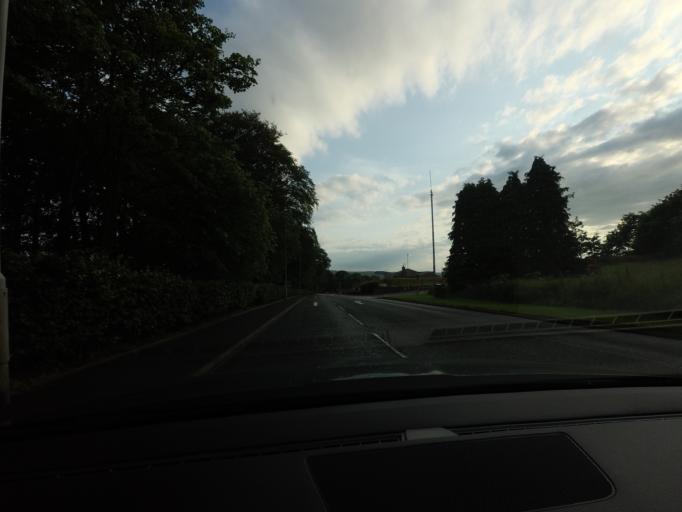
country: GB
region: Scotland
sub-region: Aberdeenshire
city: Turriff
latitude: 57.5417
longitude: -2.4507
